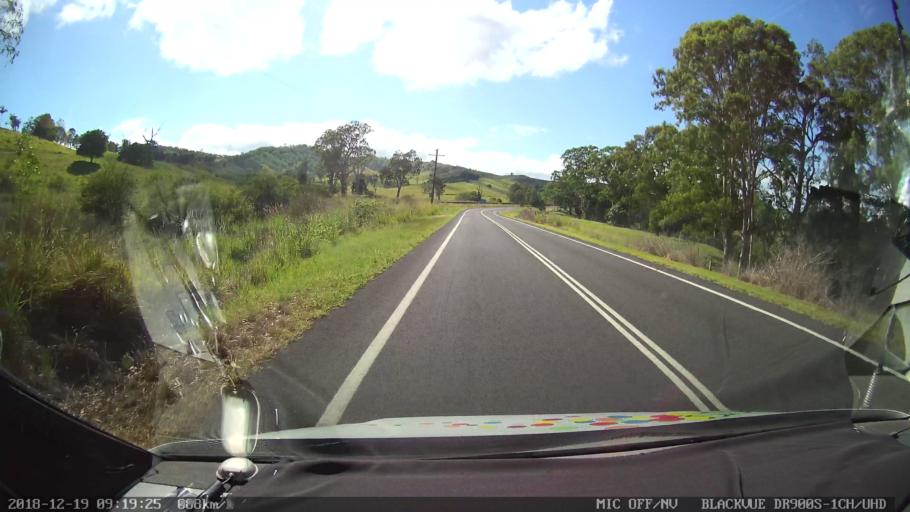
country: AU
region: New South Wales
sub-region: Kyogle
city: Kyogle
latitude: -28.5600
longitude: 152.9771
